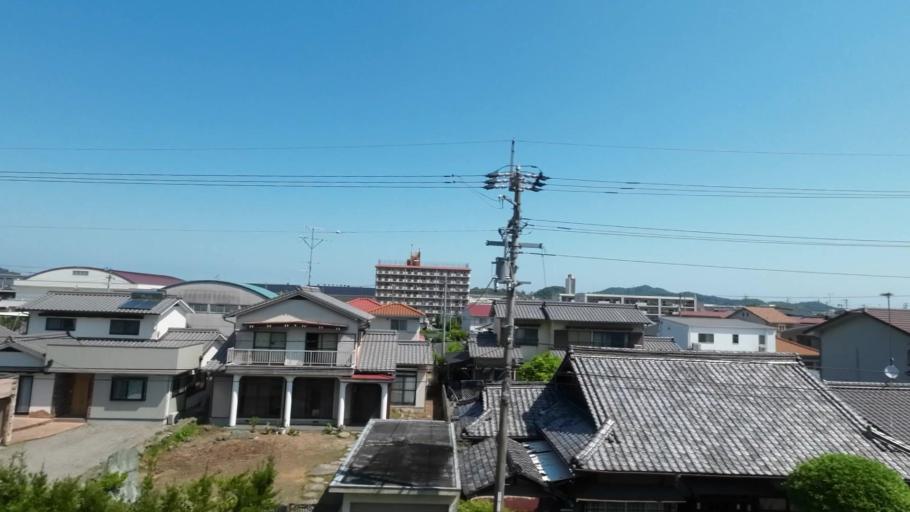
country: JP
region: Ehime
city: Niihama
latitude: 33.9738
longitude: 133.3422
